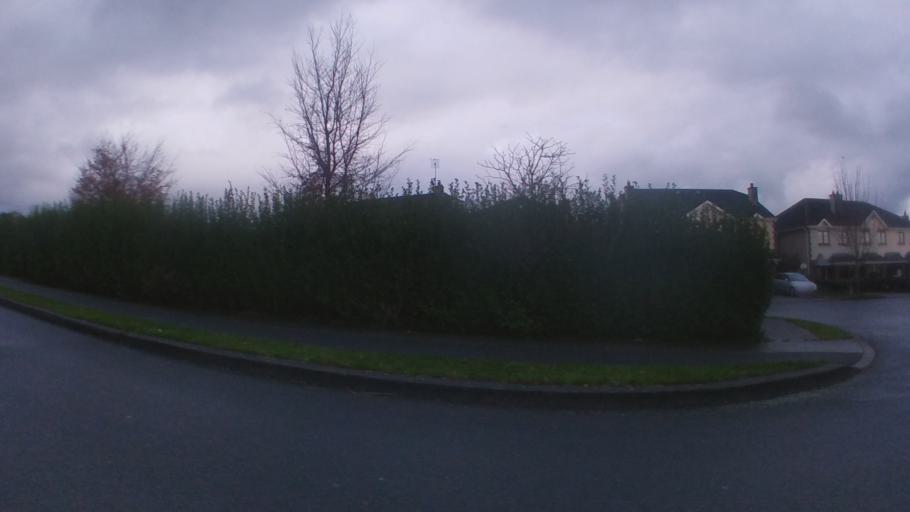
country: IE
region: Leinster
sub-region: Wicklow
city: Kilcoole
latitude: 53.1072
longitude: -6.0613
